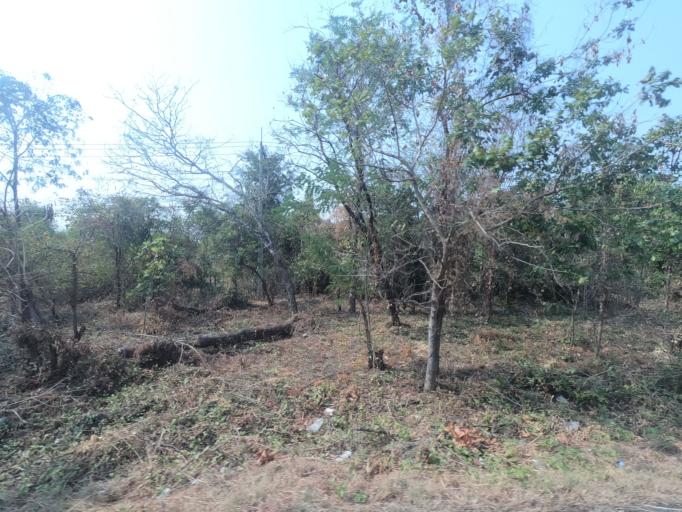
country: TH
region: Nakhon Ratchasima
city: Non Daeng
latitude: 15.3603
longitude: 102.4518
